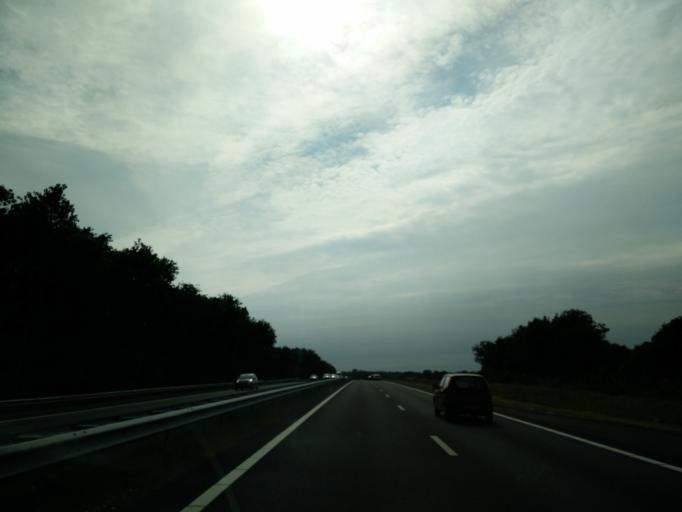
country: NL
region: Drenthe
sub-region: Gemeente Assen
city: Assen
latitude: 52.9687
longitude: 6.5880
